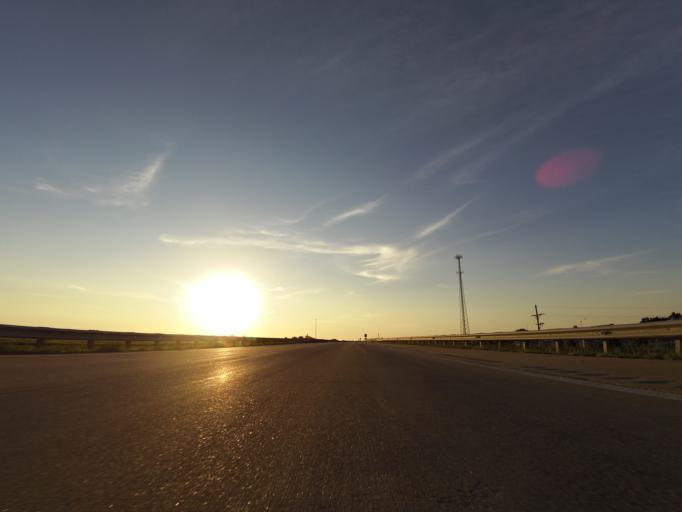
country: US
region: Kansas
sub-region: Reno County
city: Haven
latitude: 37.9360
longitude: -97.8678
